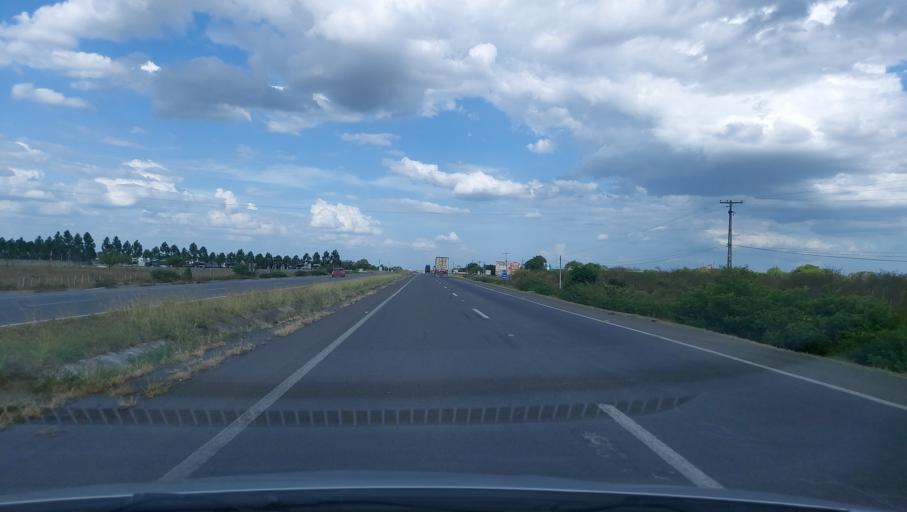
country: BR
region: Bahia
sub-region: Castro Alves
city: Castro Alves
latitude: -12.5523
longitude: -39.4563
